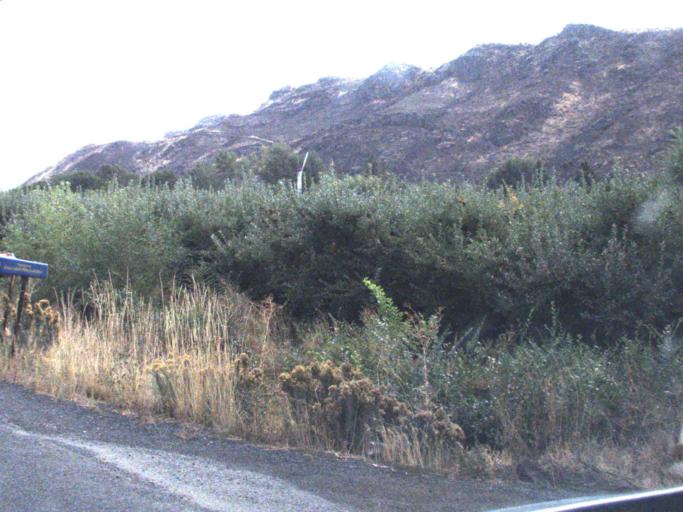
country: US
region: Washington
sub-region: Yakima County
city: Tieton
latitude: 46.7371
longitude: -120.7320
